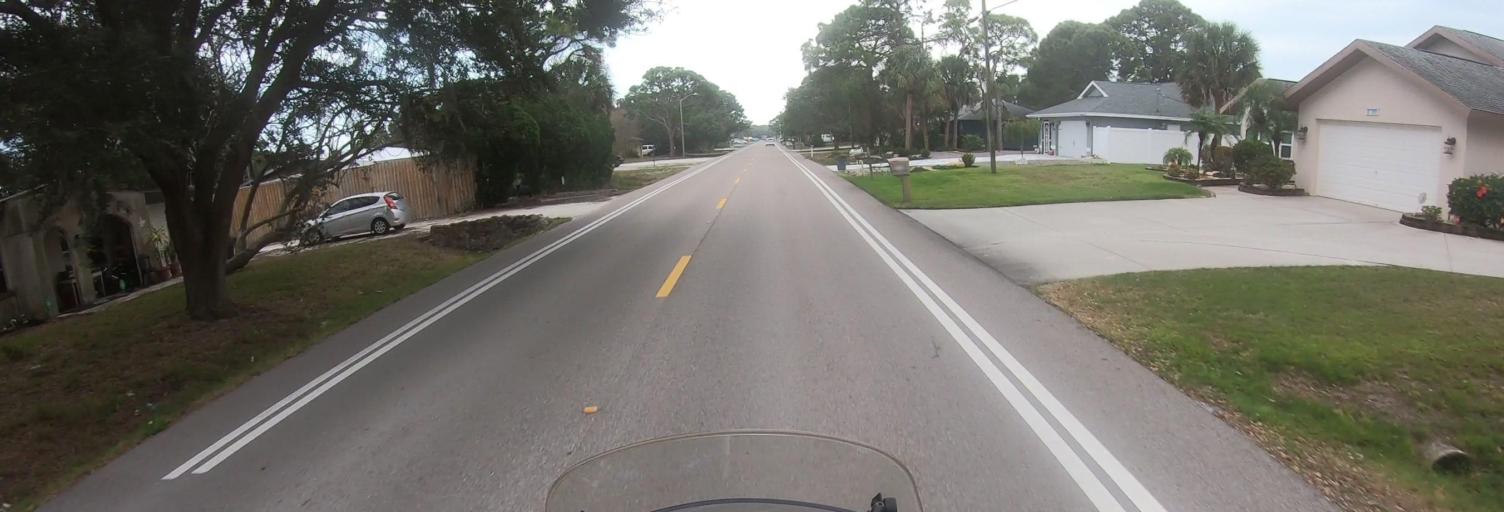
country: US
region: Florida
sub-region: Sarasota County
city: South Venice
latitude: 27.0659
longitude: -82.4291
